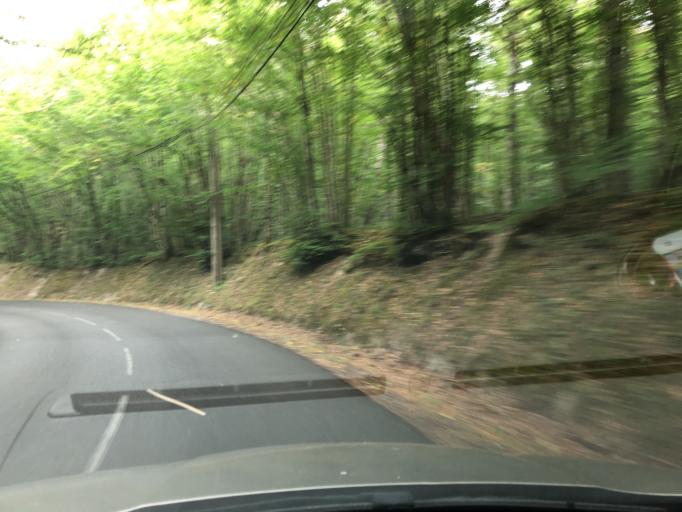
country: FR
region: Centre
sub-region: Departement d'Indre-et-Loire
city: Mazieres-de-Touraine
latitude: 47.3904
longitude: 0.4497
